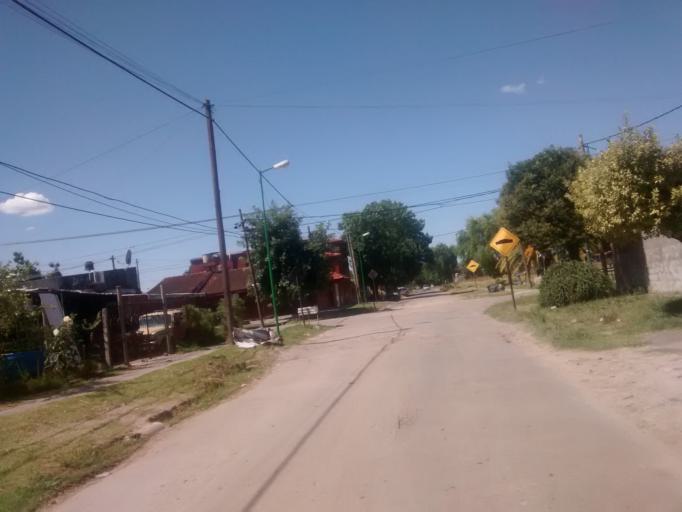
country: AR
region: Buenos Aires
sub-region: Partido de La Plata
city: La Plata
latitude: -34.9449
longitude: -57.9260
